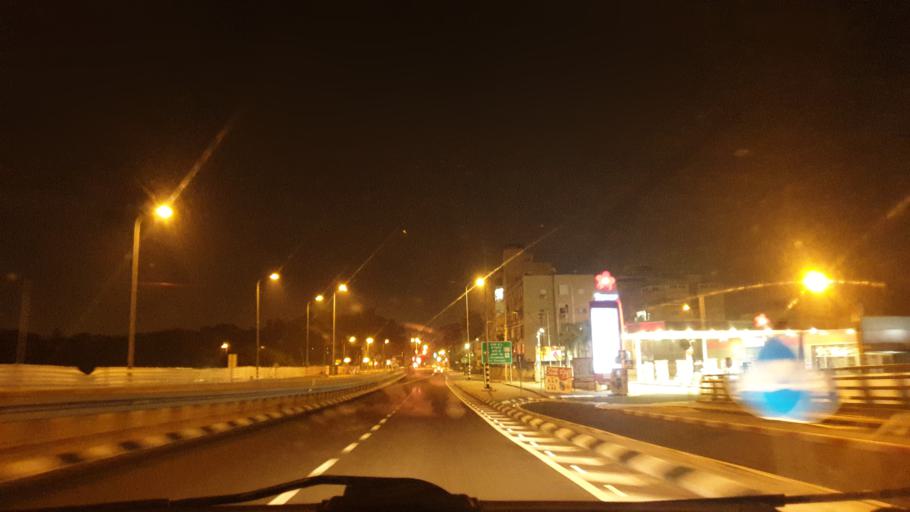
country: IL
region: Central District
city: Ramla
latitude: 31.9406
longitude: 34.8652
